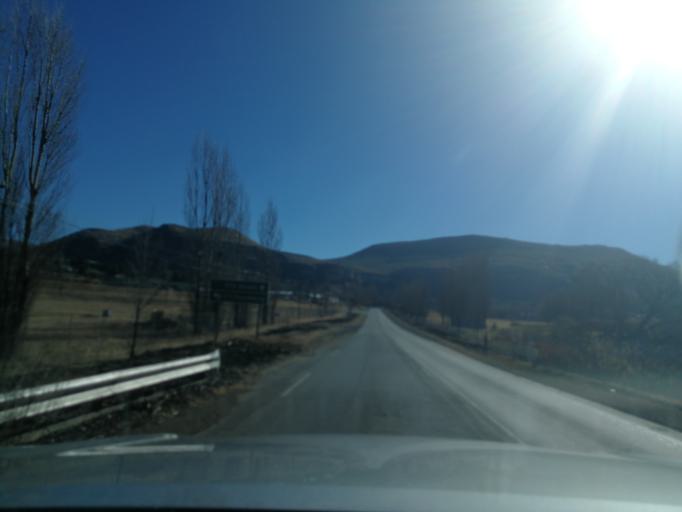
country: ZA
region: Orange Free State
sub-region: Thabo Mofutsanyana District Municipality
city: Bethlehem
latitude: -28.5131
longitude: 28.4296
